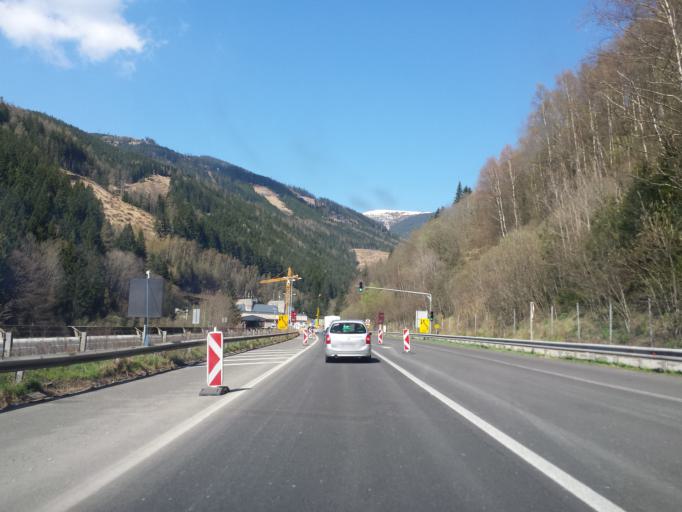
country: AT
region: Styria
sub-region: Politischer Bezirk Graz-Umgebung
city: Ubelbach
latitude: 47.2482
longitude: 15.1646
